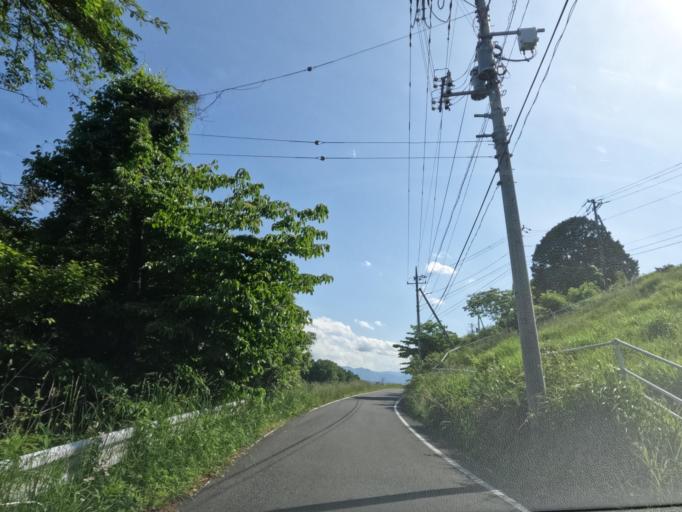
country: JP
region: Saitama
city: Yorii
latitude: 36.0488
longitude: 139.1584
